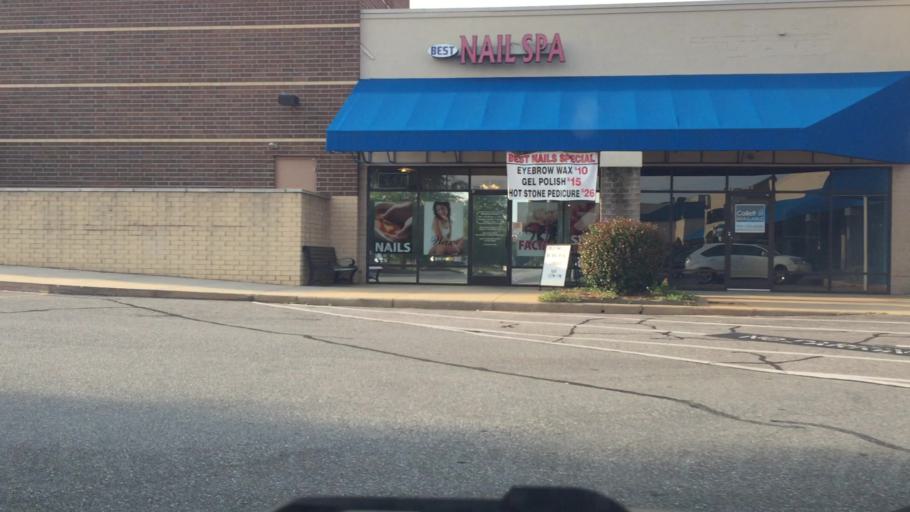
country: US
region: North Carolina
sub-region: Iredell County
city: Mooresville
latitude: 35.5951
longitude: -80.8544
